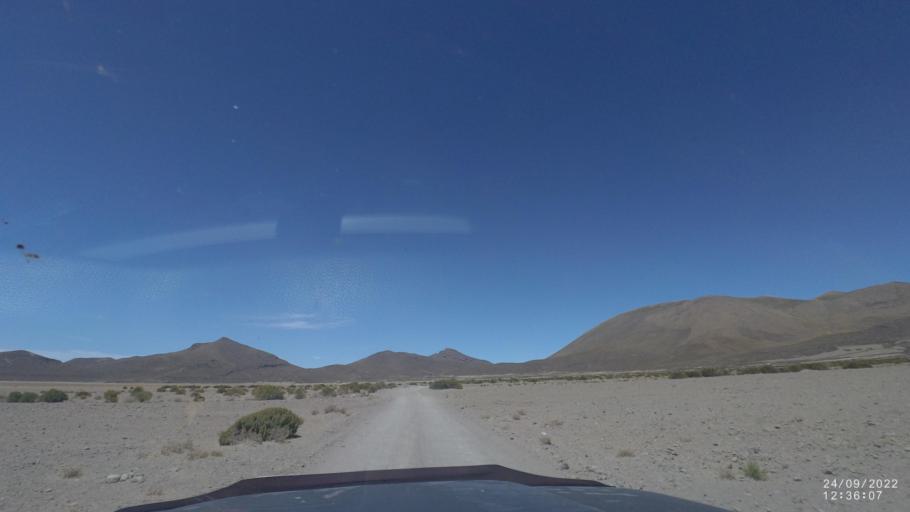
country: BO
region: Potosi
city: Colchani
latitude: -19.7852
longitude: -67.5899
